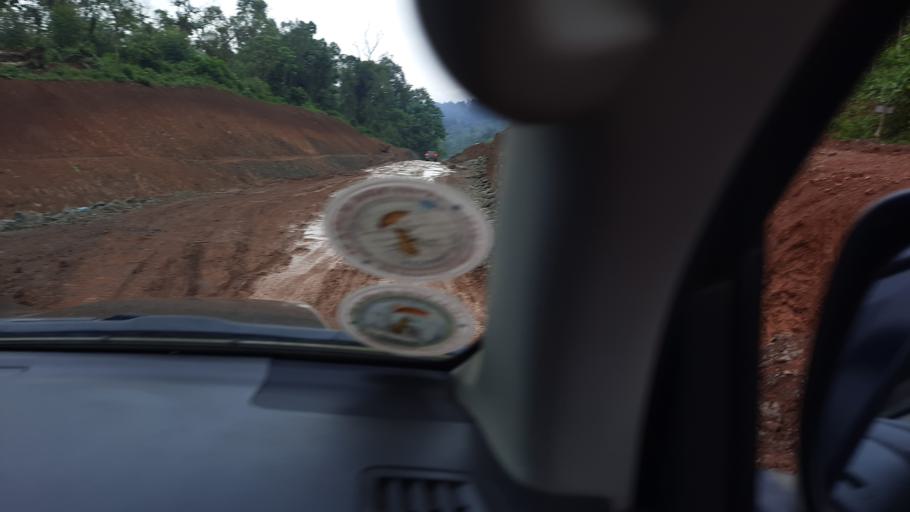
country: ET
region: Oromiya
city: Gore
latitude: 7.8652
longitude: 35.4800
